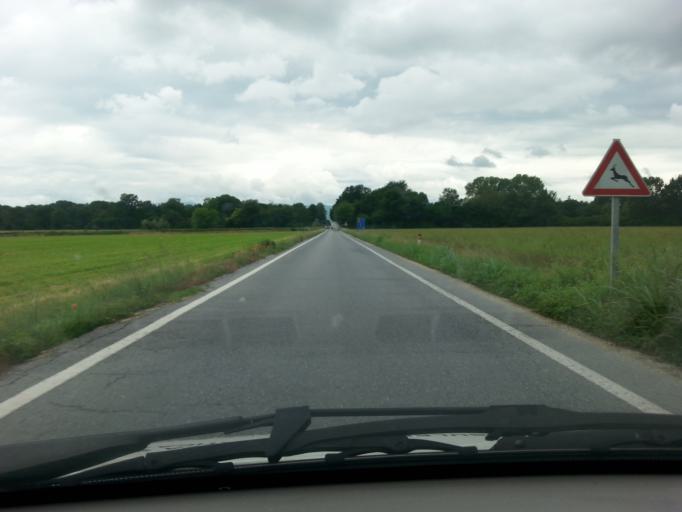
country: IT
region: Piedmont
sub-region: Provincia di Torino
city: Garino
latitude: 44.9957
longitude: 7.6003
